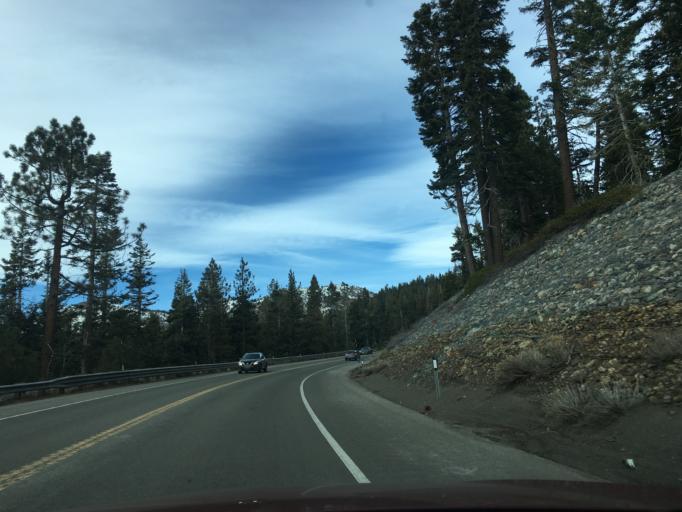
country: US
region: Nevada
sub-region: Washoe County
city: Incline Village
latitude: 39.2646
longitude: -119.9296
